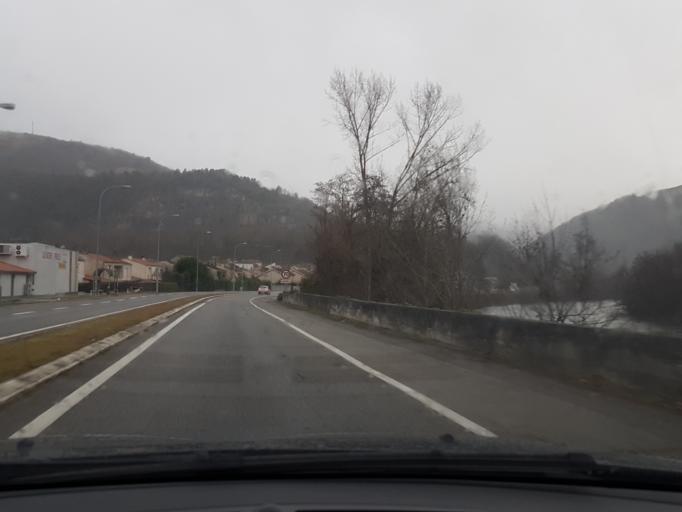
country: FR
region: Midi-Pyrenees
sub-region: Departement de l'Ariege
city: Foix
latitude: 42.9869
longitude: 1.6156
